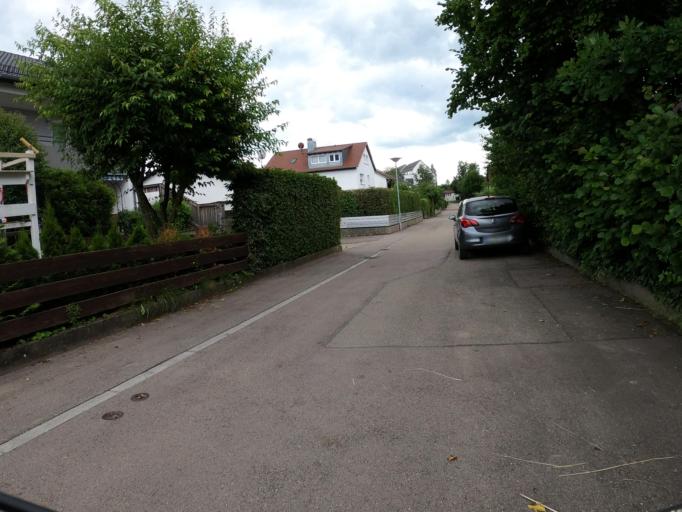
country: DE
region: Baden-Wuerttemberg
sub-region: Tuebingen Region
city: Langenau
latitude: 48.5028
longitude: 10.1196
